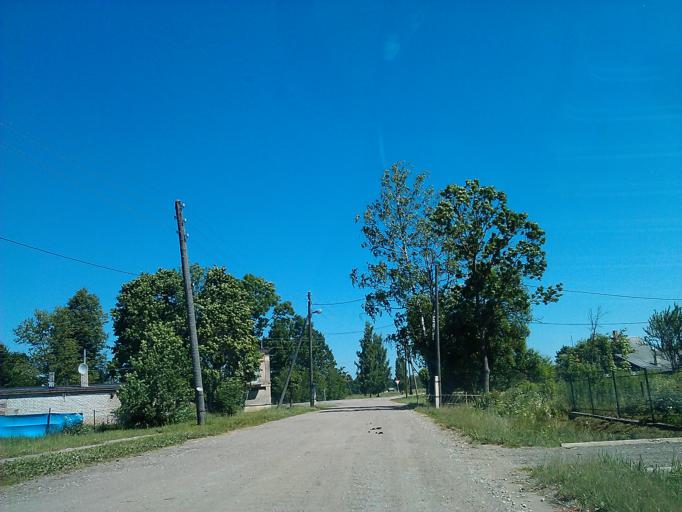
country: LV
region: Vilanu
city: Vilani
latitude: 56.5494
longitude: 26.9273
